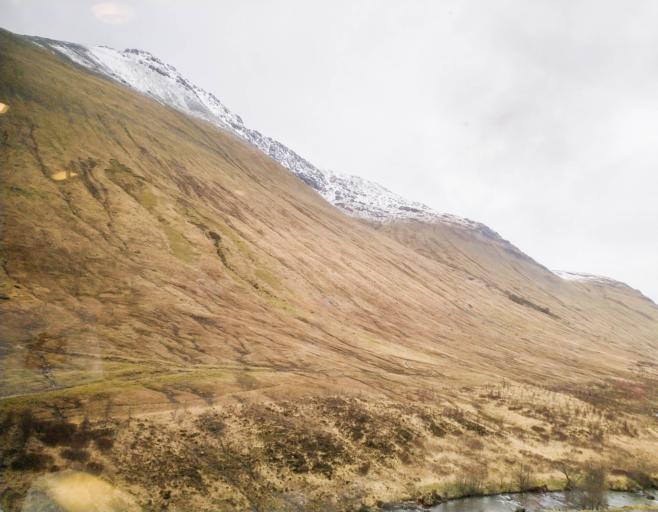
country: GB
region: Scotland
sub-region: Argyll and Bute
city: Garelochhead
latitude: 56.4891
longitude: -4.7052
